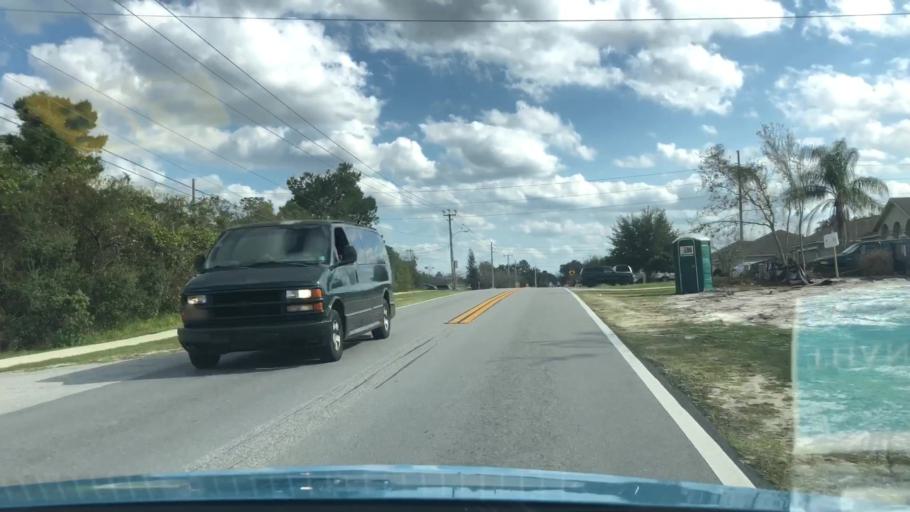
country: US
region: Florida
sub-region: Volusia County
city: Lake Helen
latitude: 28.9350
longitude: -81.1784
